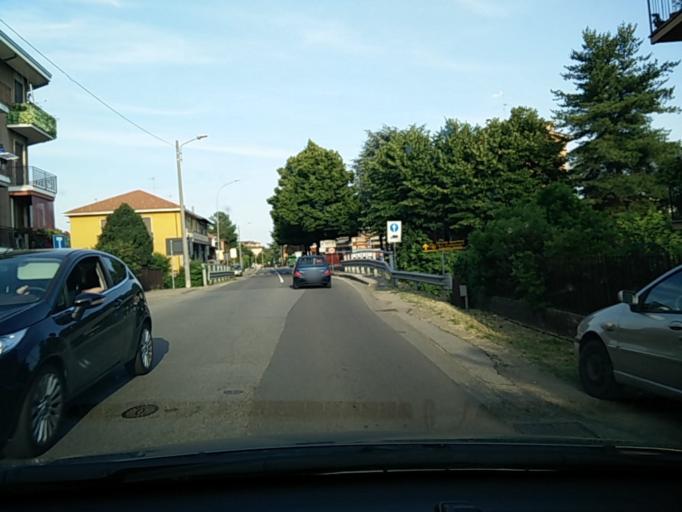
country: IT
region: Lombardy
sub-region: Provincia di Pavia
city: San Martino Siccomario
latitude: 45.1643
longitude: 9.1417
